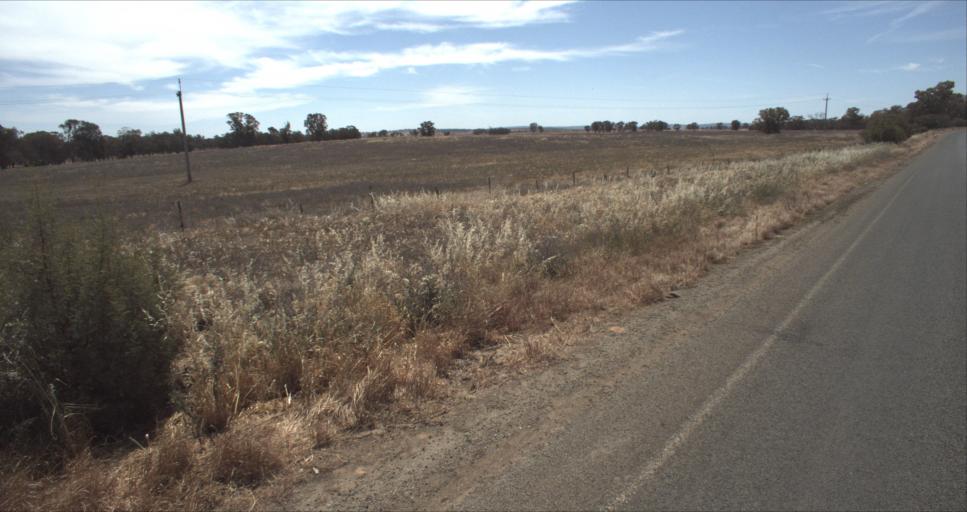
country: AU
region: New South Wales
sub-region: Leeton
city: Leeton
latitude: -34.6616
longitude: 146.4509
